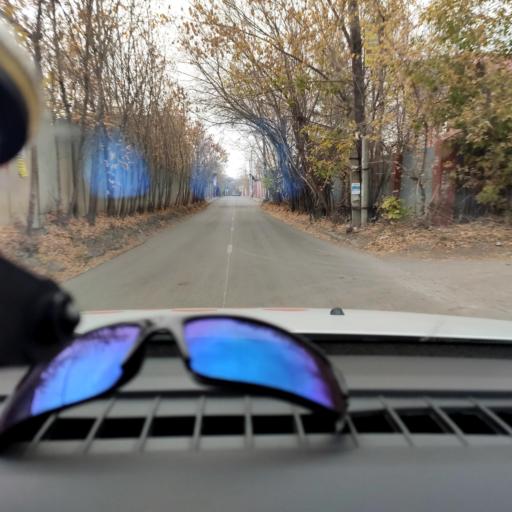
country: RU
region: Samara
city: Samara
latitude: 53.2350
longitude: 50.1770
